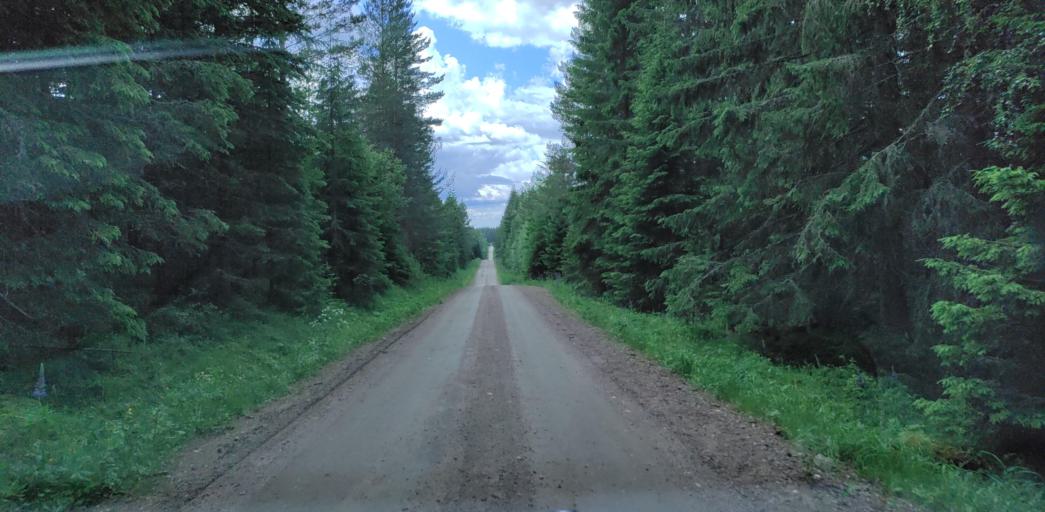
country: SE
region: Vaermland
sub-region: Hagfors Kommun
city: Ekshaerad
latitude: 60.0901
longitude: 13.3365
